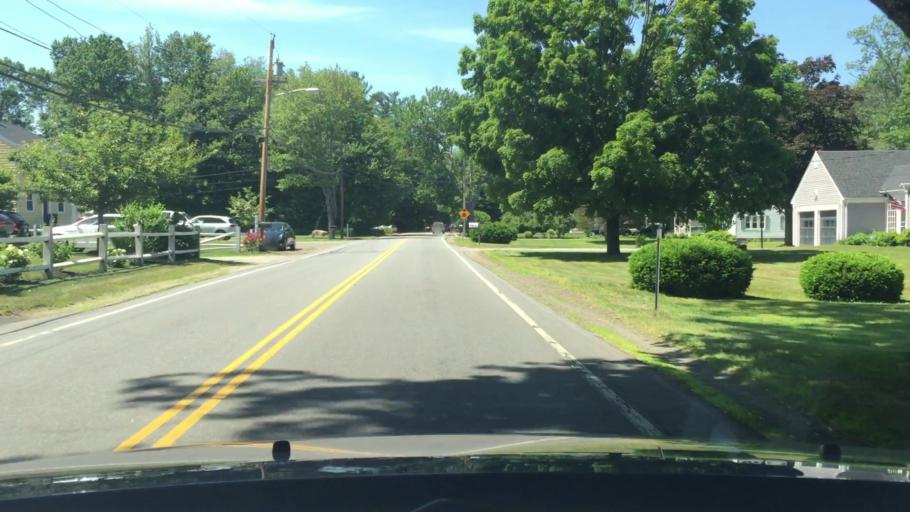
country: US
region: New Hampshire
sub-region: Rockingham County
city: Plaistow
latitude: 42.8157
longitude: -71.0947
